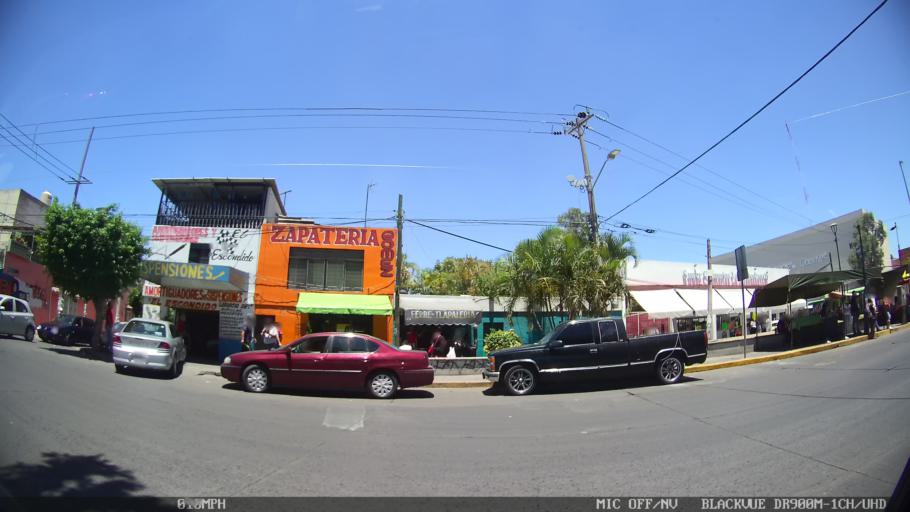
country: MX
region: Jalisco
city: Tlaquepaque
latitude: 20.6608
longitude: -103.2770
